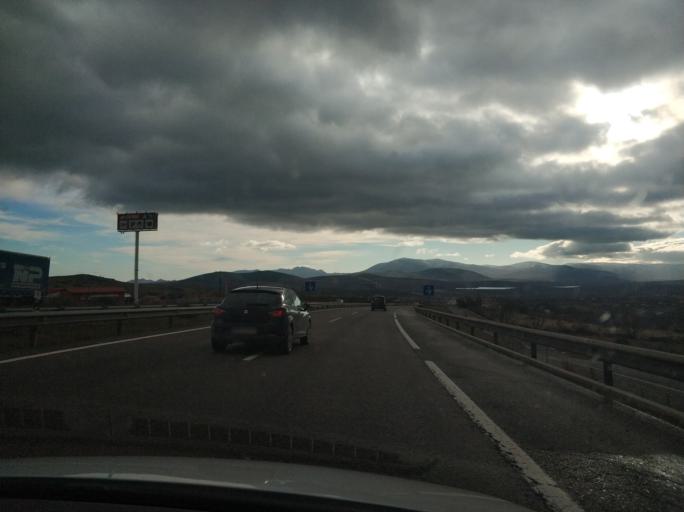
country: ES
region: Madrid
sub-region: Provincia de Madrid
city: Braojos
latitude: 41.0364
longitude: -3.6179
